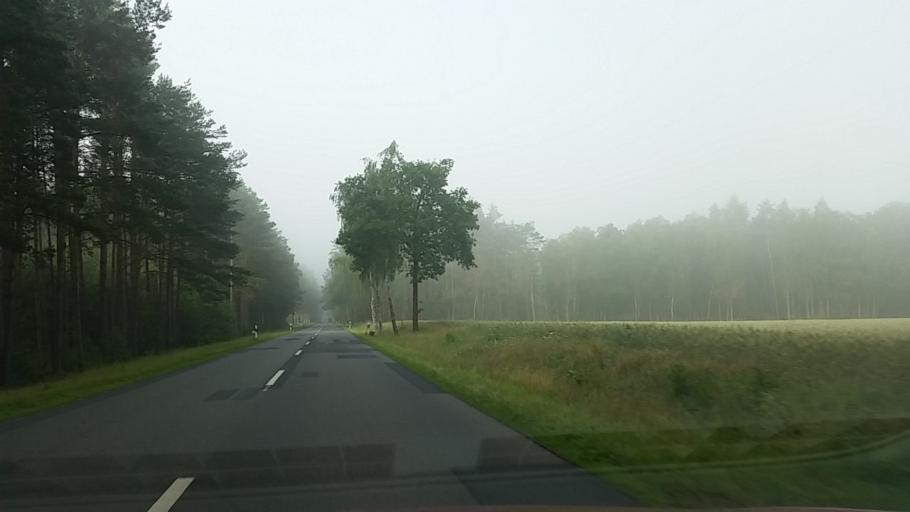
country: DE
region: Lower Saxony
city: Schoneworde
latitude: 52.6355
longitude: 10.6941
